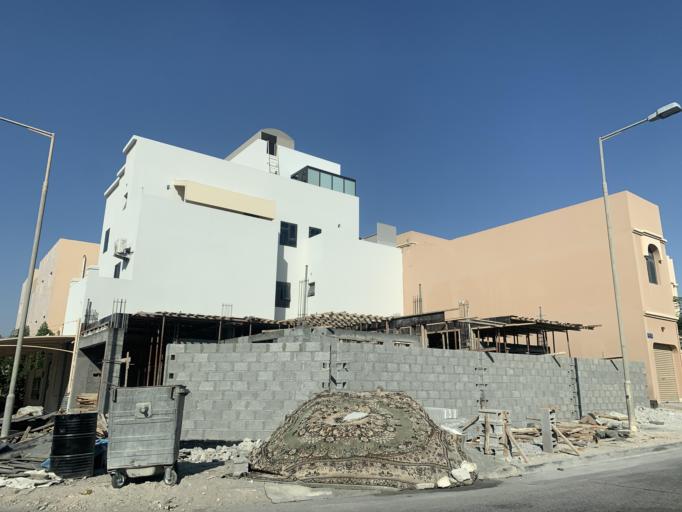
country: BH
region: Central Governorate
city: Madinat Hamad
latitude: 26.1011
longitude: 50.5086
